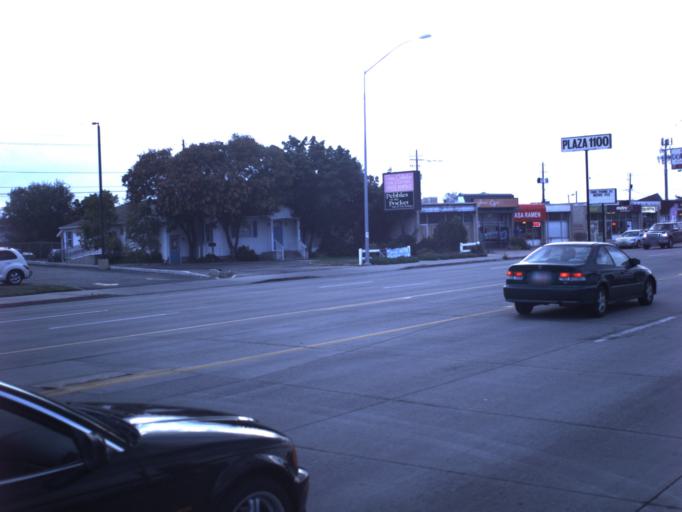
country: US
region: Utah
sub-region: Utah County
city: Orem
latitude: 40.2762
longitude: -111.6857
